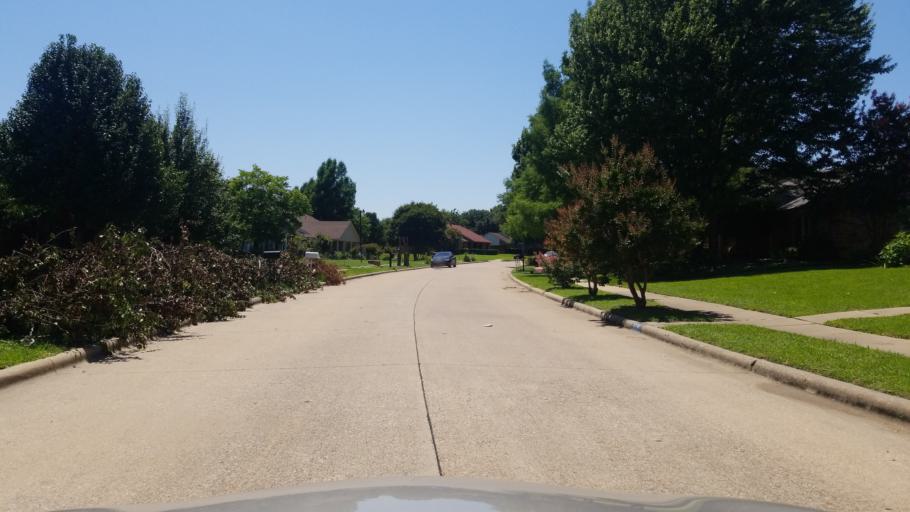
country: US
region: Texas
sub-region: Dallas County
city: Grand Prairie
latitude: 32.6847
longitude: -97.0028
